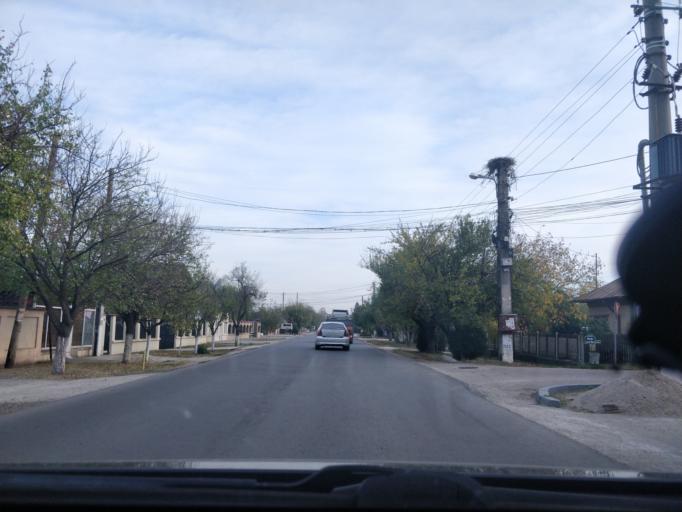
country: RO
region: Giurgiu
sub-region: Comuna Bolintin Vale
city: Malu Spart
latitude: 44.4388
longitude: 25.7192
